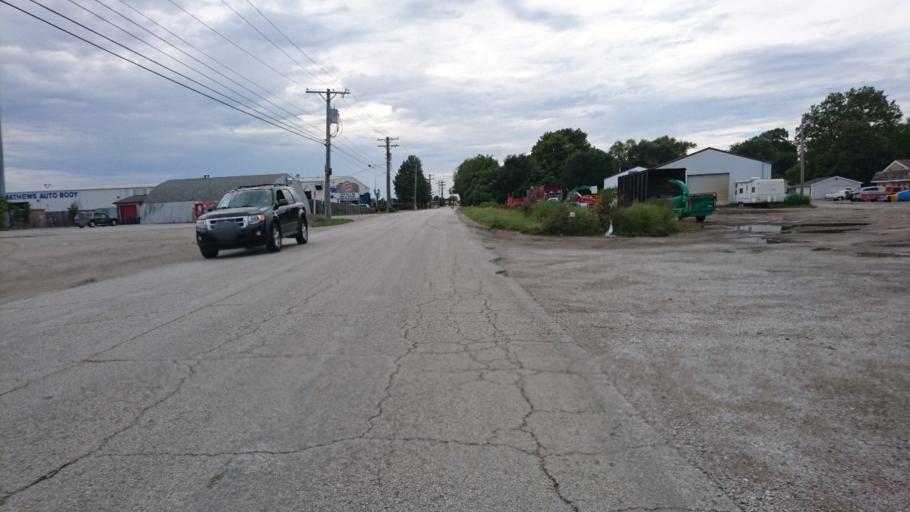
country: US
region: Illinois
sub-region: Sangamon County
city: Southern View
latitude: 39.7666
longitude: -89.6628
